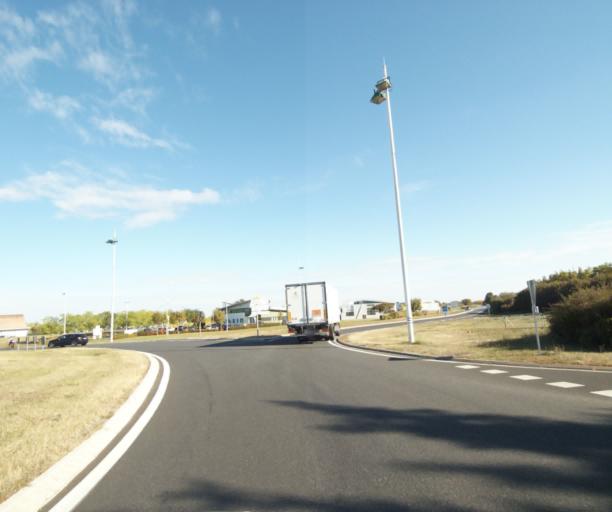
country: FR
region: Auvergne
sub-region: Departement du Puy-de-Dome
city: Gerzat
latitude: 45.8462
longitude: 3.1671
